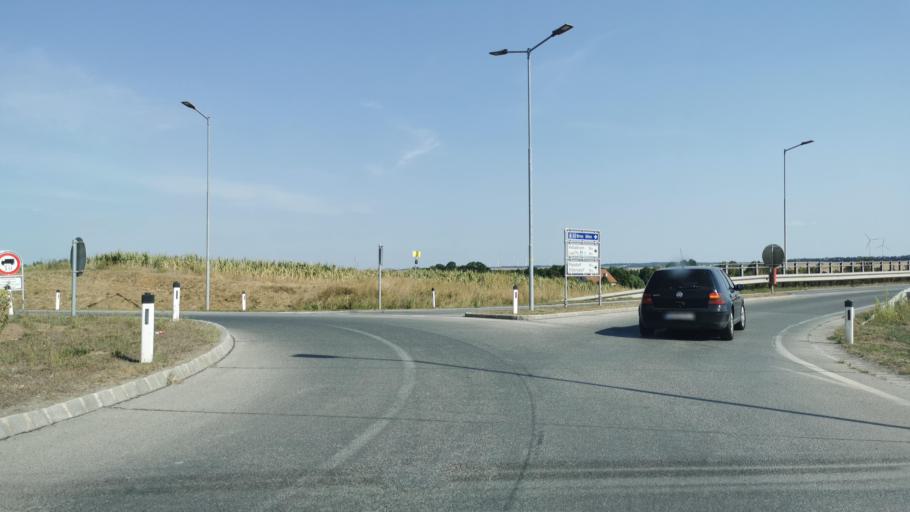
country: AT
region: Lower Austria
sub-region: Politischer Bezirk Mistelbach
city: Mistelbach
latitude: 48.5711
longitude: 16.6059
